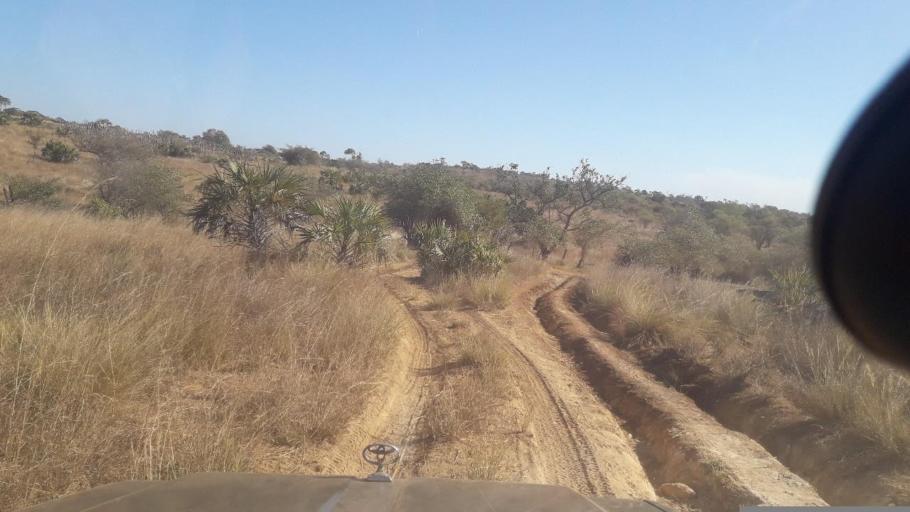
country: MG
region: Boeny
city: Sitampiky
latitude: -16.3759
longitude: 45.5905
